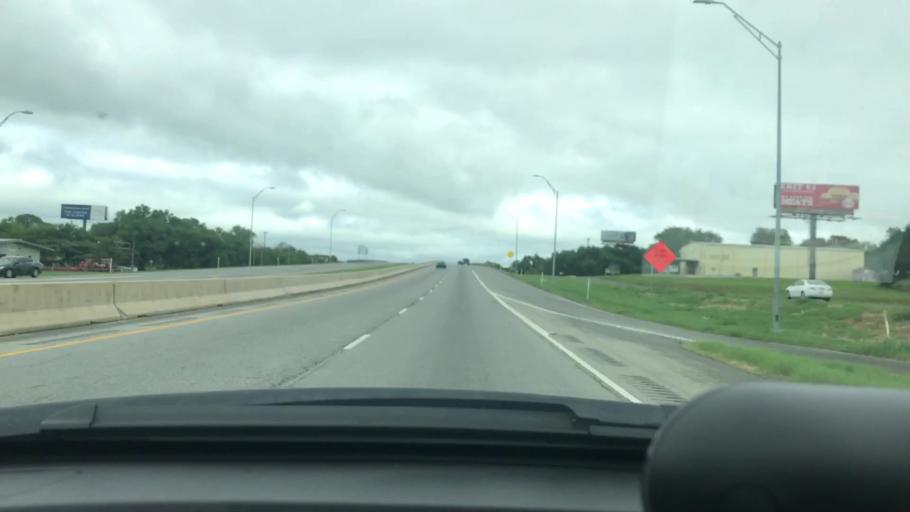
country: US
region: Texas
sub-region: Grayson County
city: Sherman
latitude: 33.6257
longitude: -96.6126
